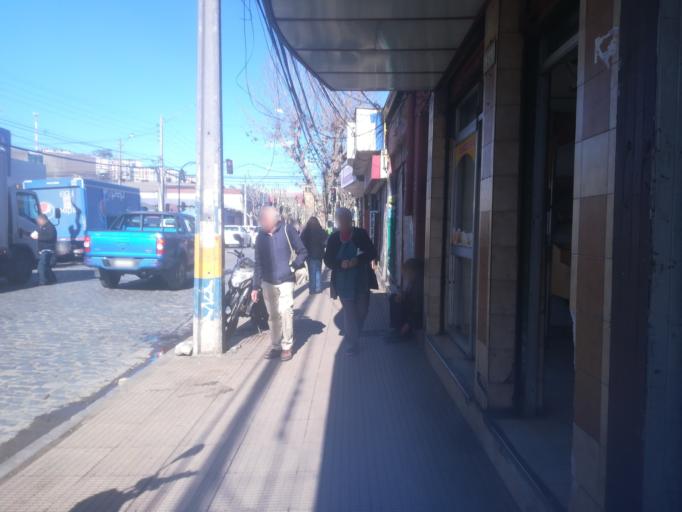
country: CL
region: Valparaiso
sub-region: Provincia de Valparaiso
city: Vina del Mar
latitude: -33.0105
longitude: -71.5426
